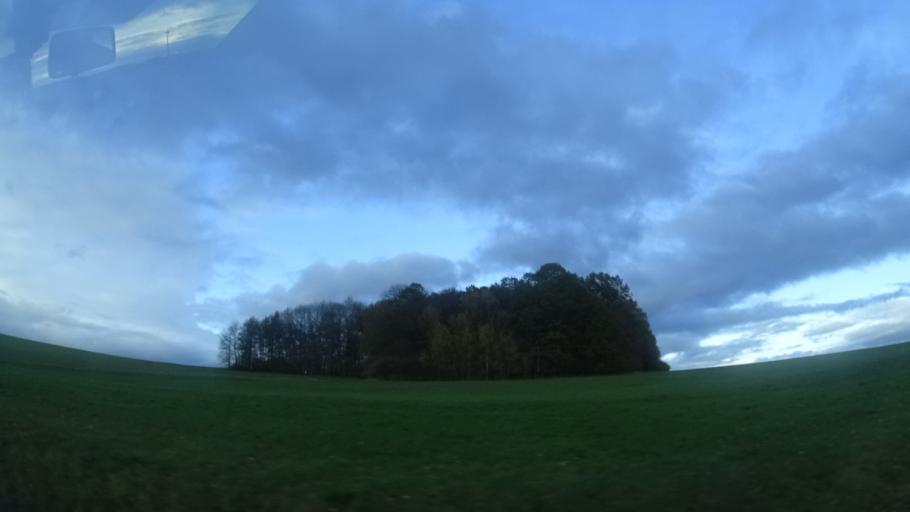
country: DE
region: Hesse
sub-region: Regierungsbezirk Giessen
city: Freiensteinau
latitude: 50.4562
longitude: 9.4381
